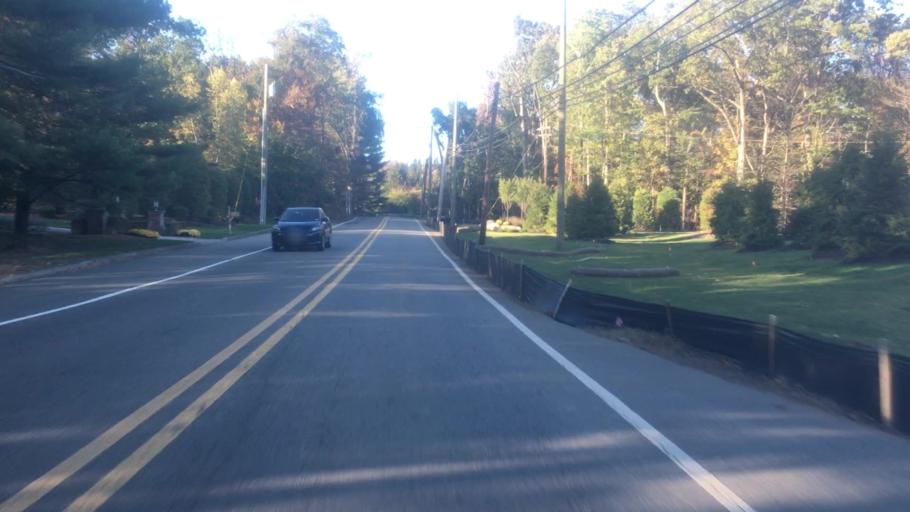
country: US
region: New Jersey
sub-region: Bergen County
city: Franklin Lakes
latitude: 40.9889
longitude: -74.1999
